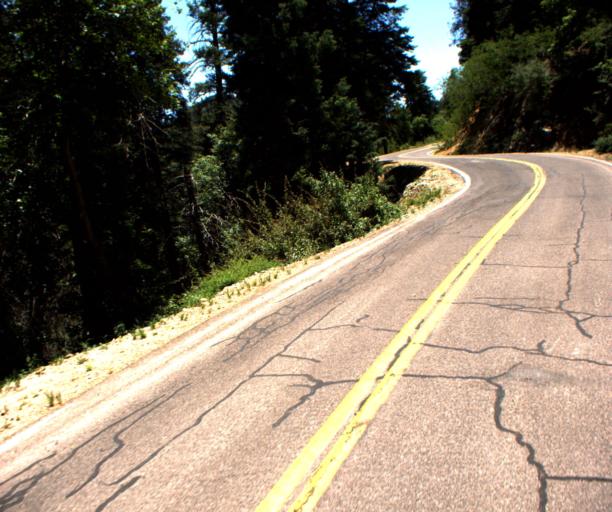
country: US
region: Arizona
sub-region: Graham County
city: Swift Trail Junction
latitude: 32.6259
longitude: -109.8282
